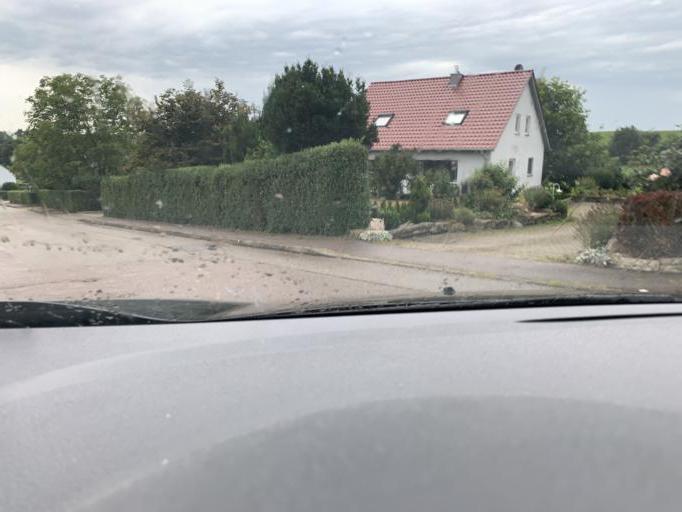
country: DE
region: Baden-Wuerttemberg
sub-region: Regierungsbezirk Stuttgart
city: Schwaebisch Hall
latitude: 49.1337
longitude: 9.7553
